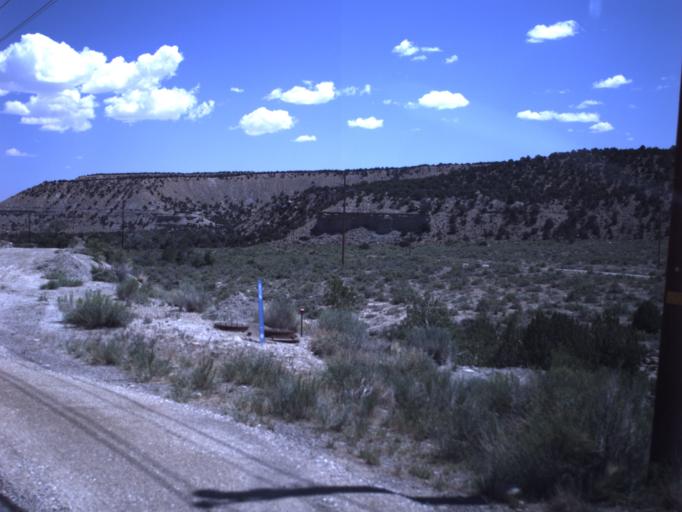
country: US
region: Utah
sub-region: Emery County
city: Orangeville
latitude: 39.2695
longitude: -111.1478
